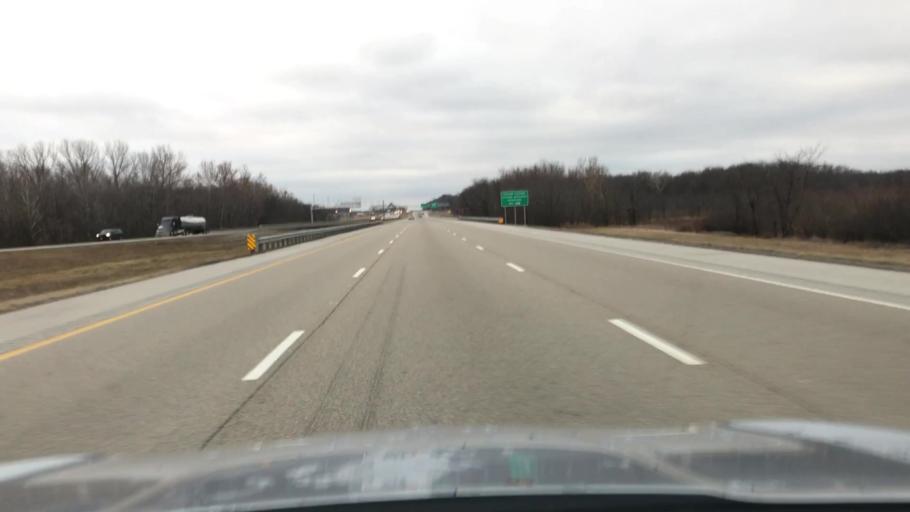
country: US
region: Illinois
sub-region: Logan County
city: Lincoln
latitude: 40.1706
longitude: -89.4180
